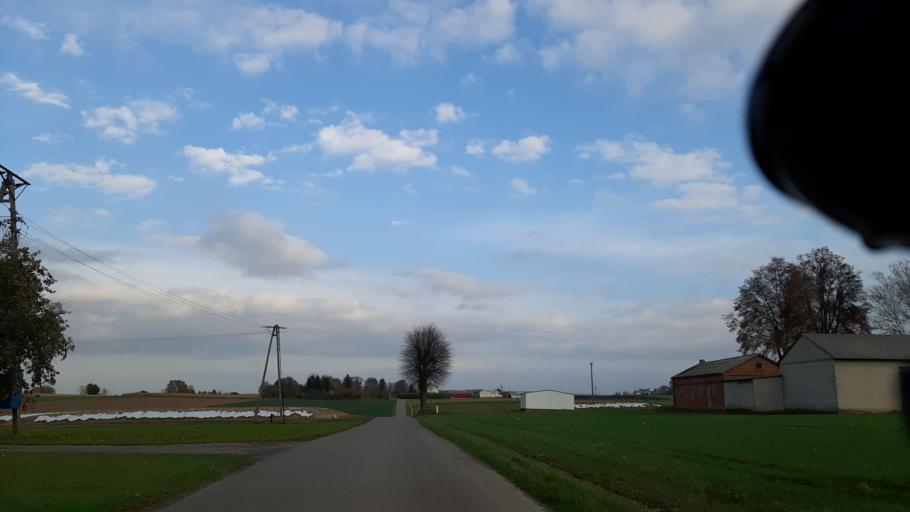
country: PL
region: Lublin Voivodeship
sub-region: Powiat pulawski
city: Markuszow
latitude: 51.3319
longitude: 22.2568
